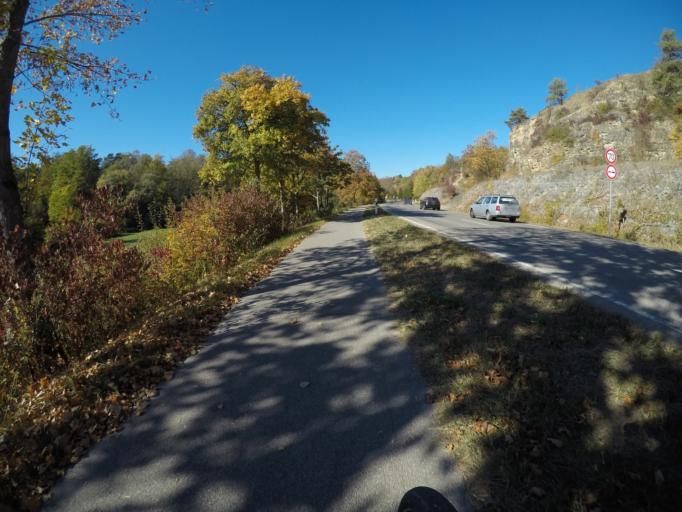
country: DE
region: Baden-Wuerttemberg
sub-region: Tuebingen Region
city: Rottenburg
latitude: 48.5386
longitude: 8.9305
